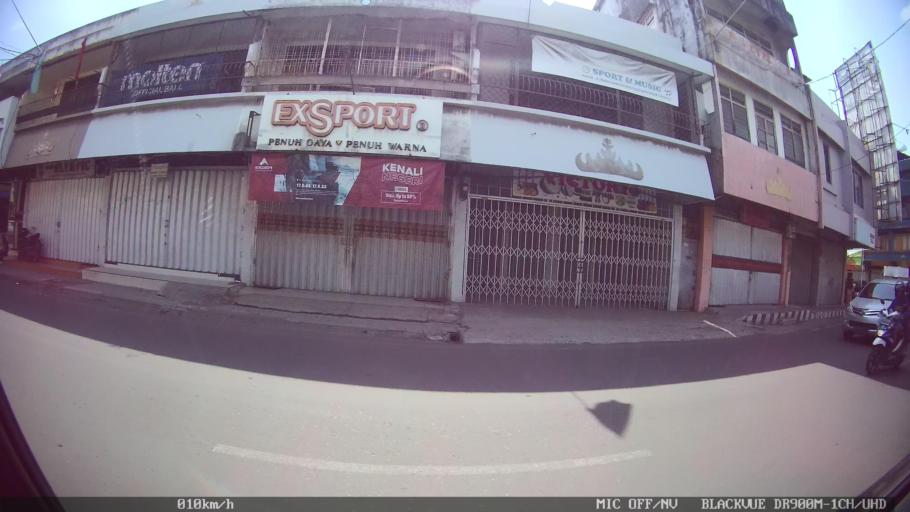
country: ID
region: Lampung
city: Bandarlampung
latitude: -5.4117
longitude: 105.2583
